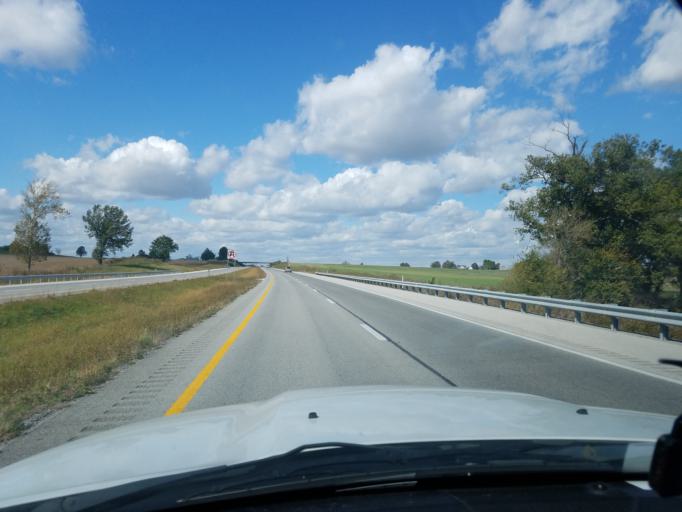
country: US
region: Kentucky
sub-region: Daviess County
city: Masonville
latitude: 37.6569
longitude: -87.0071
